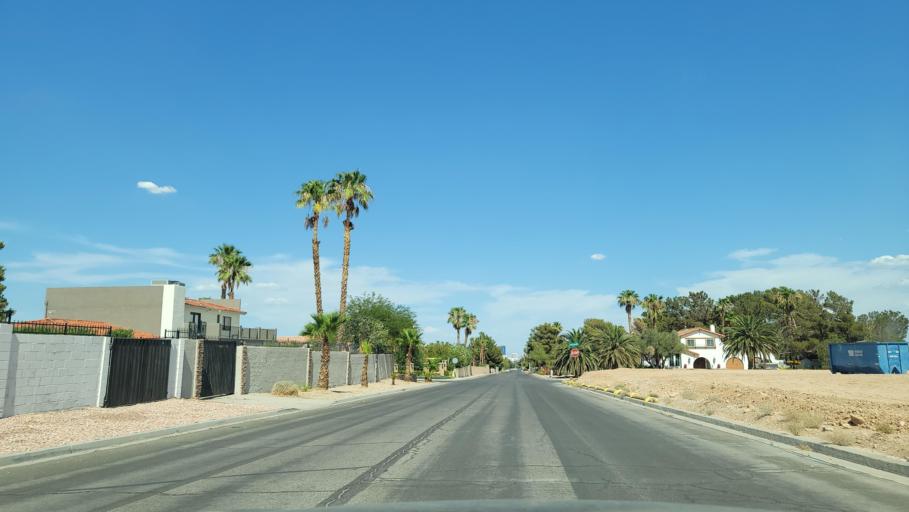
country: US
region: Nevada
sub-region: Clark County
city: Spring Valley
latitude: 36.1348
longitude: -115.2530
